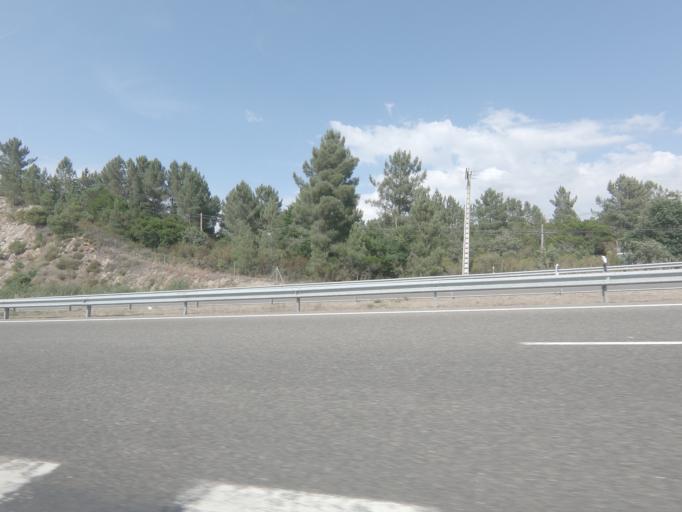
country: ES
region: Galicia
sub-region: Provincia de Ourense
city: Ourense
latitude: 42.2822
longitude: -7.8735
